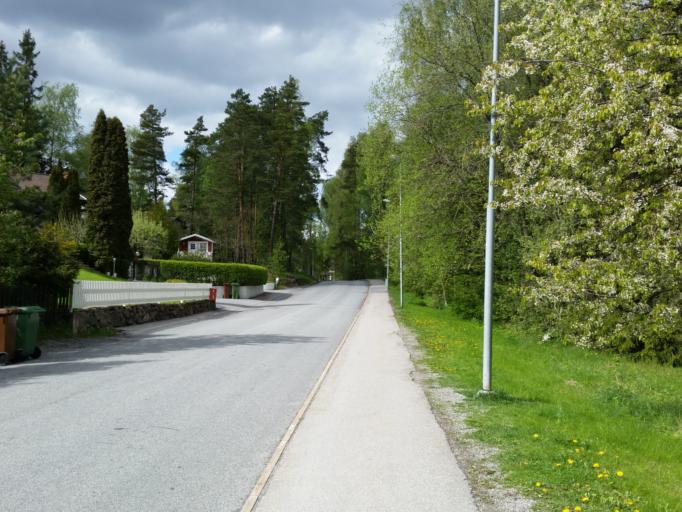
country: SE
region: Stockholm
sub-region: Sollentuna Kommun
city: Sollentuna
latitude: 59.4580
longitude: 17.9496
